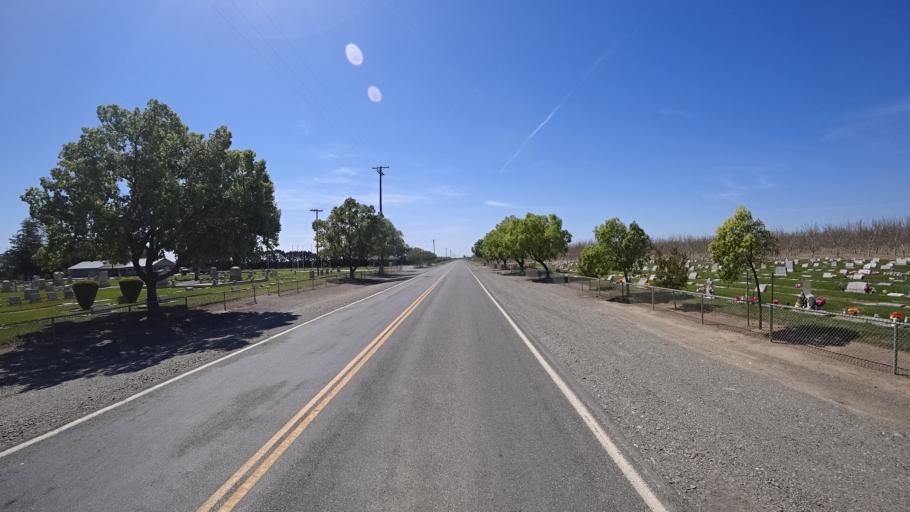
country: US
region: California
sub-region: Glenn County
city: Orland
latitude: 39.7034
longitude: -122.1406
